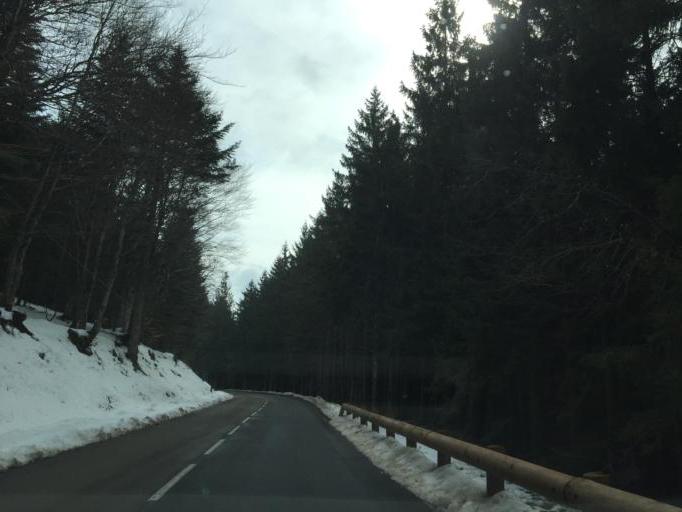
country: FR
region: Rhone-Alpes
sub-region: Departement de la Loire
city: Bourg-Argental
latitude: 45.3762
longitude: 4.5276
